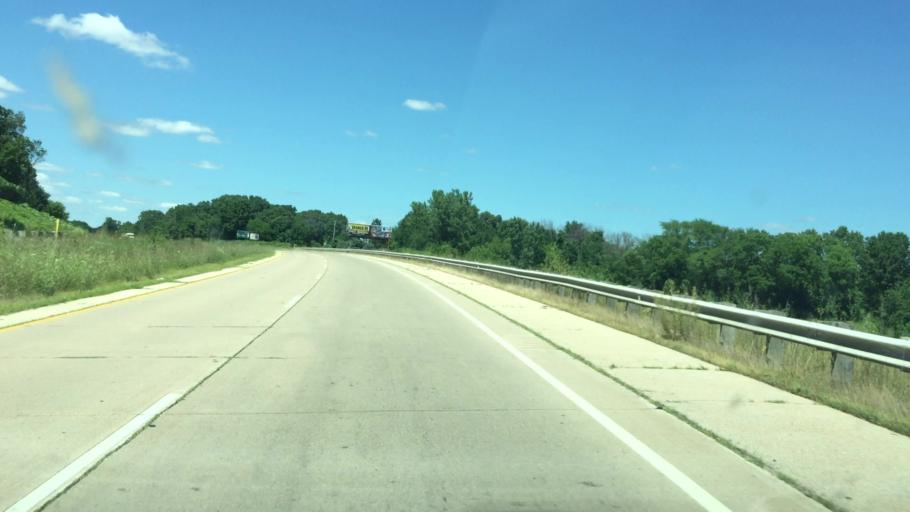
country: US
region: Illinois
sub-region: Jo Daviess County
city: East Dubuque
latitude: 42.5431
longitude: -90.6072
